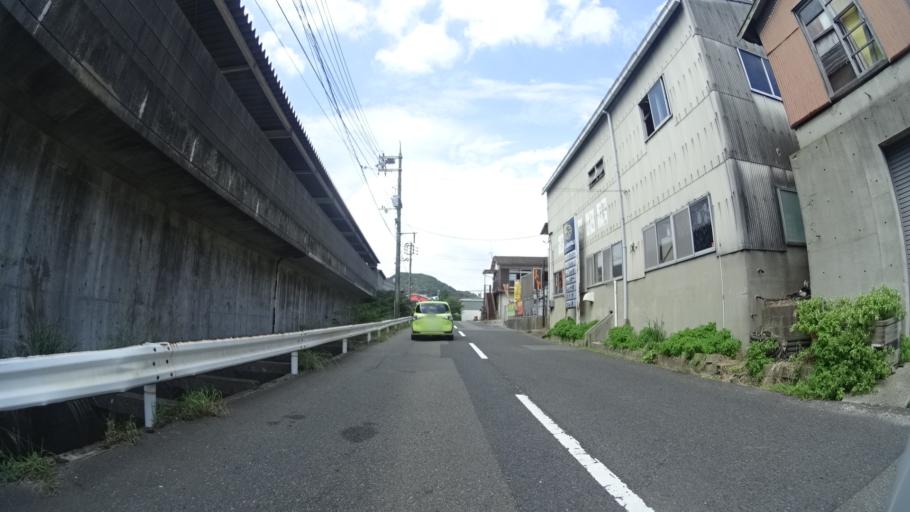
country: JP
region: Yamaguchi
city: Shimonoseki
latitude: 33.9786
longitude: 130.9510
